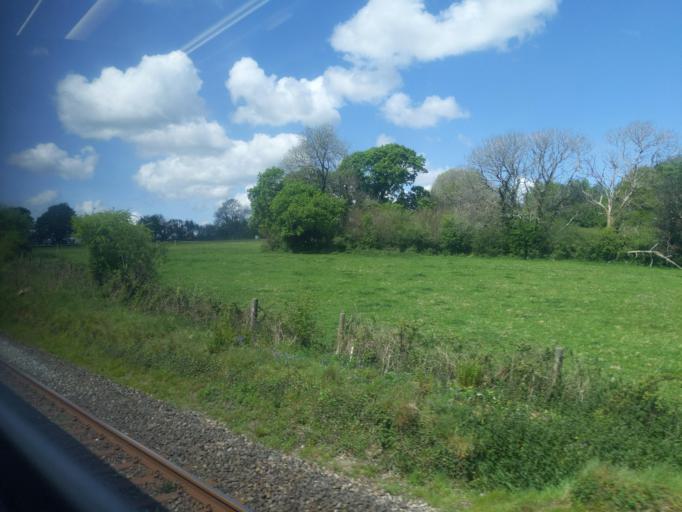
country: GB
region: England
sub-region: Cornwall
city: Liskeard
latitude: 50.4201
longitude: -4.3851
